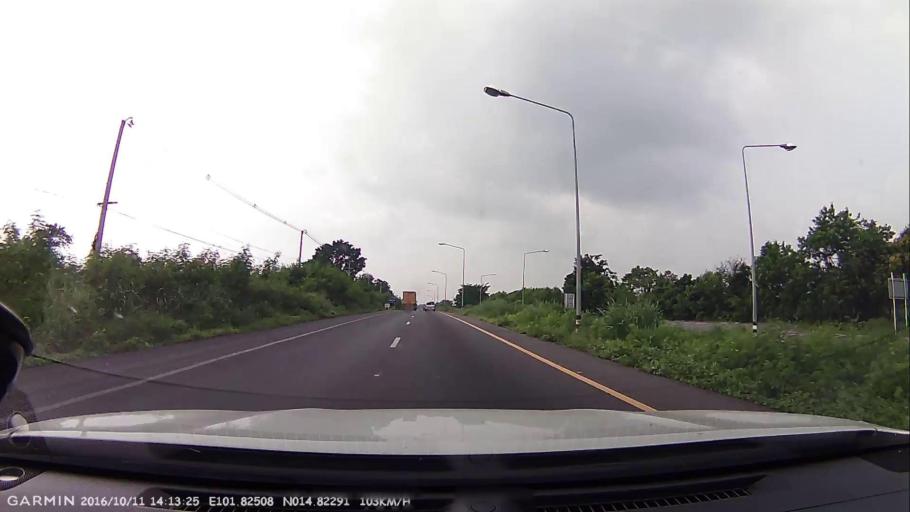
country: TH
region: Nakhon Ratchasima
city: Sung Noen
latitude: 14.8229
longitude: 101.8250
